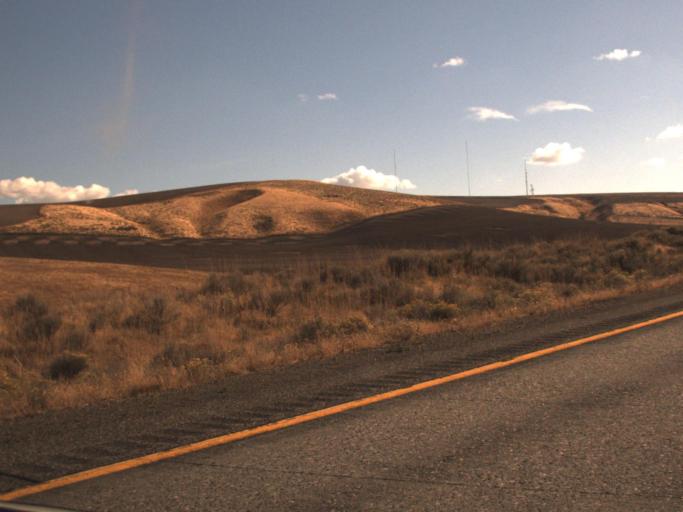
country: US
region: Washington
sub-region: Benton County
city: Highland
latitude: 46.1173
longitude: -119.2032
